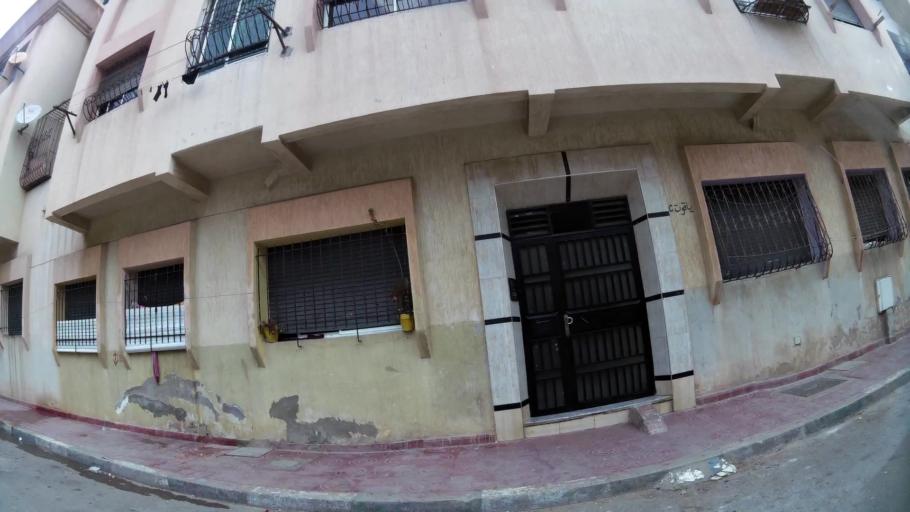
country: MA
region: Rabat-Sale-Zemmour-Zaer
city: Sale
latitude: 34.0640
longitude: -6.7859
